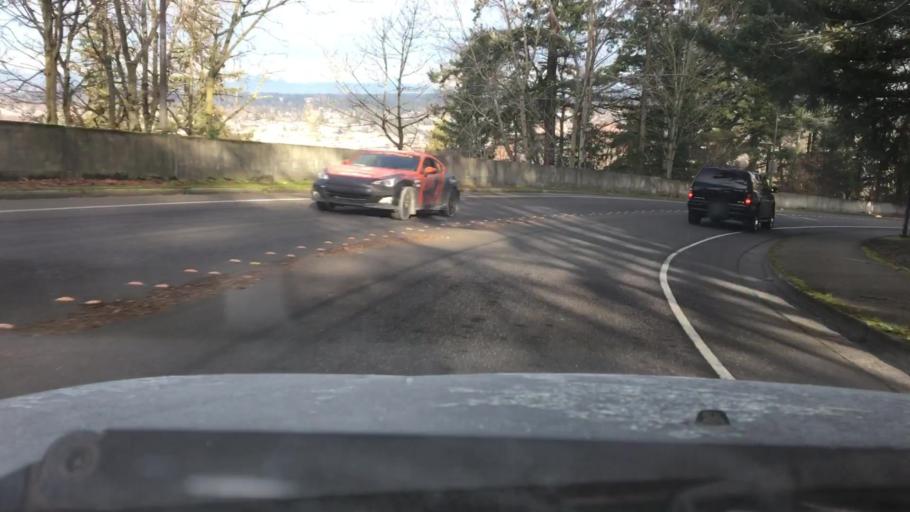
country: US
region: Washington
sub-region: Whatcom County
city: Bellingham
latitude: 48.7378
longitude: -122.4884
